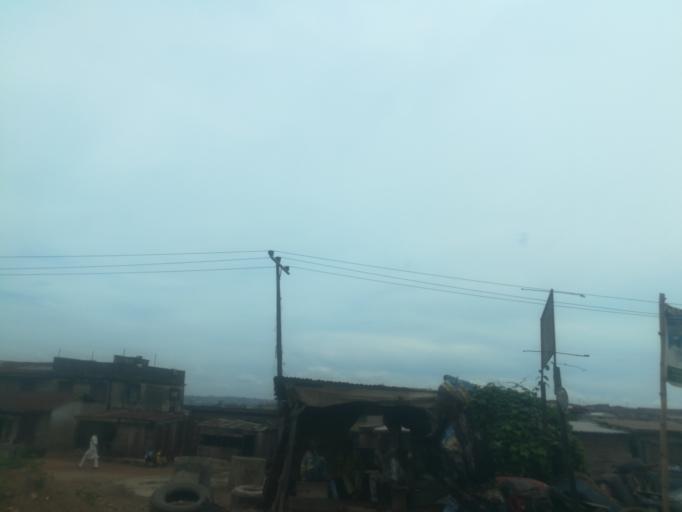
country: NG
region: Oyo
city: Ibadan
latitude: 7.3670
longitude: 3.9279
